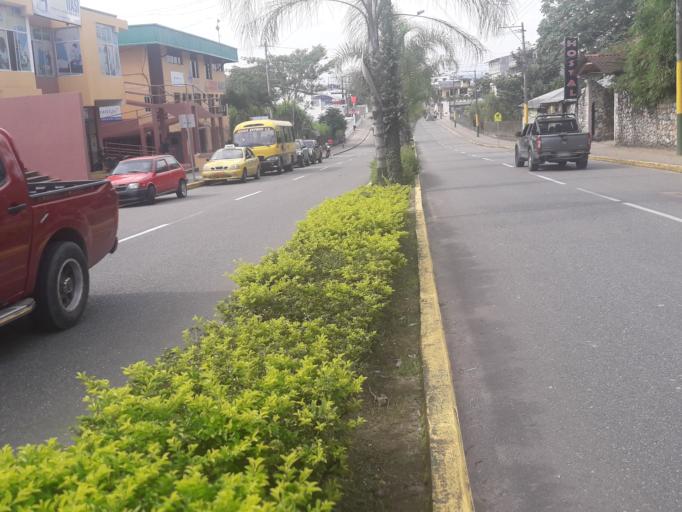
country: EC
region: Napo
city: Tena
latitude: -0.9868
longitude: -77.8133
